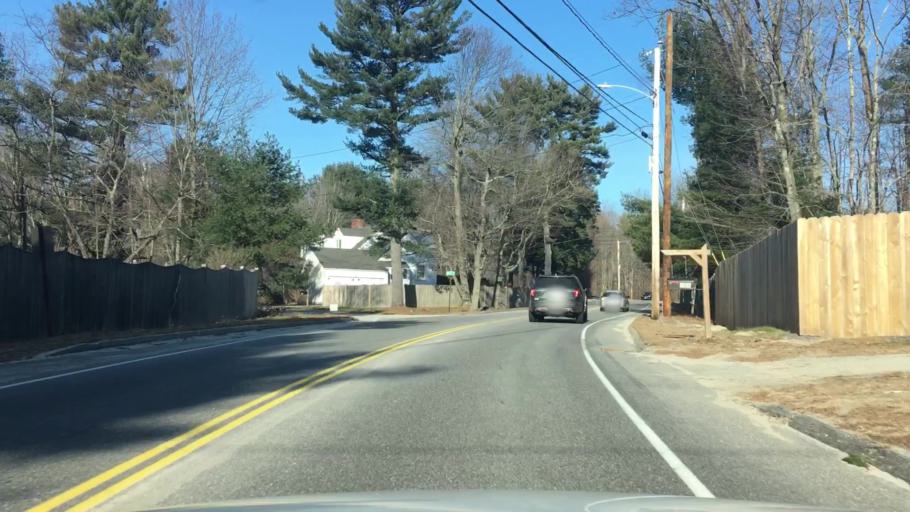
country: US
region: Maine
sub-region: Cumberland County
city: Falmouth
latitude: 43.7193
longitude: -70.2639
